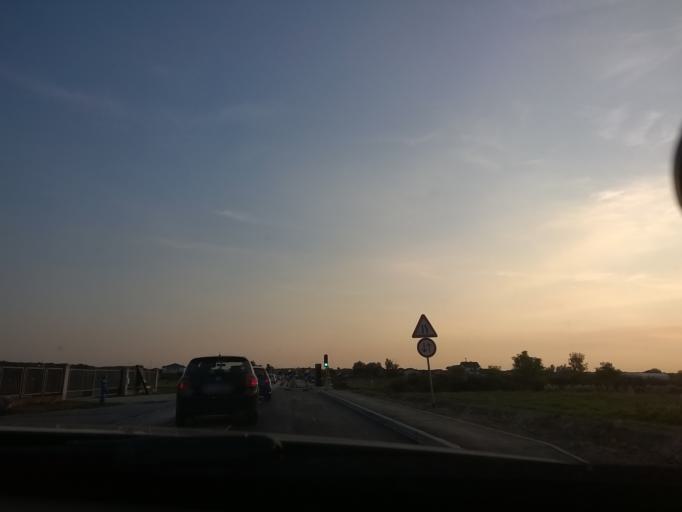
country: HR
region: Grad Zagreb
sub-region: Sesvete
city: Sesvete
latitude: 45.8615
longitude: 16.1514
